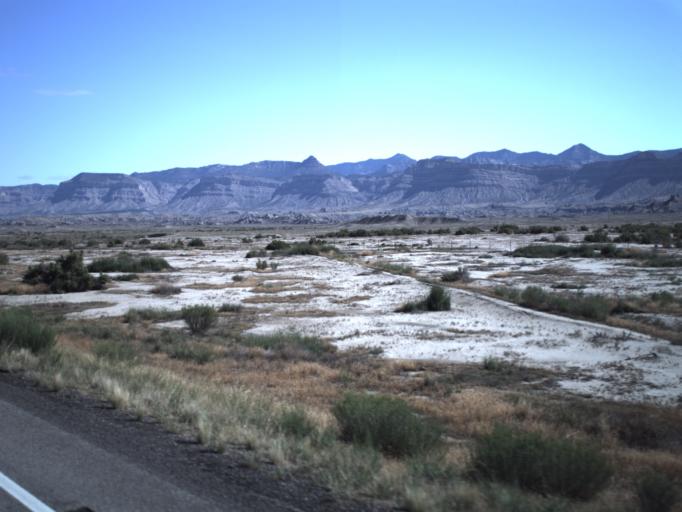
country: US
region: Utah
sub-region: Carbon County
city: East Carbon City
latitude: 39.3282
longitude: -110.3676
